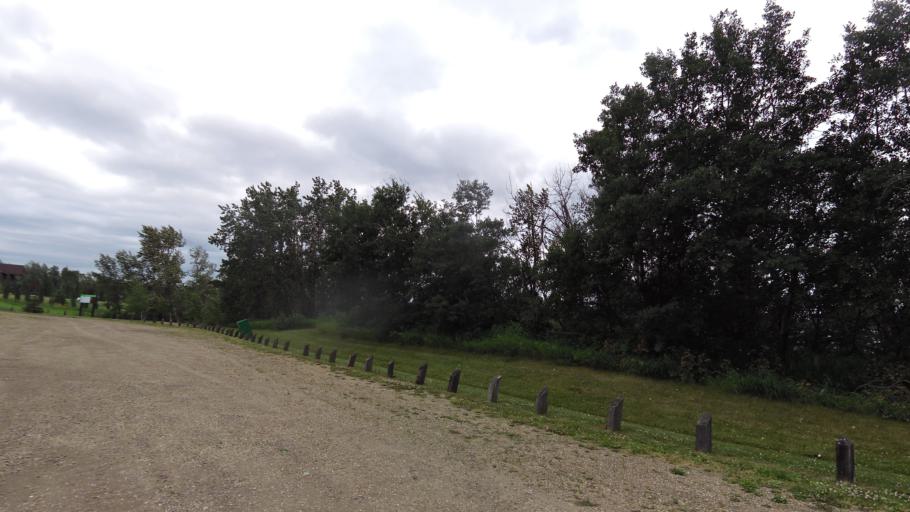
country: CA
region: Alberta
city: Stony Plain
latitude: 53.4901
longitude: -114.2273
